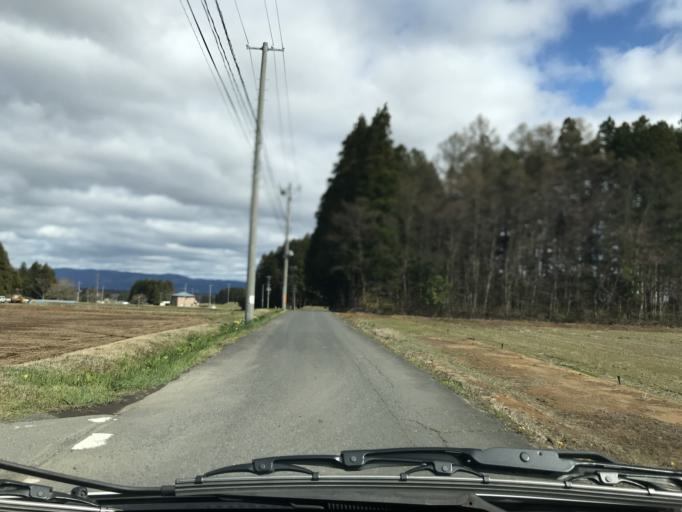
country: JP
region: Iwate
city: Mizusawa
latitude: 39.1064
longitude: 141.0256
